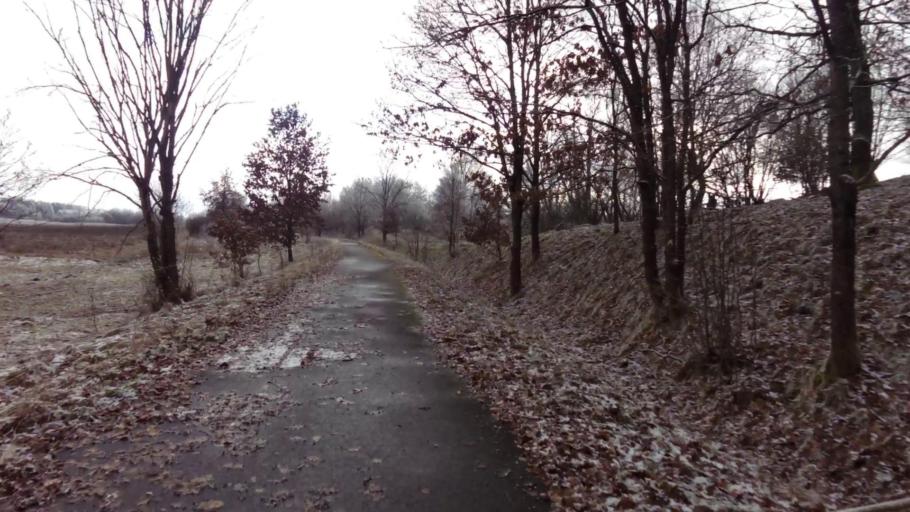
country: PL
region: West Pomeranian Voivodeship
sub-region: Powiat drawski
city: Zlocieniec
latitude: 53.6497
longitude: 16.0396
